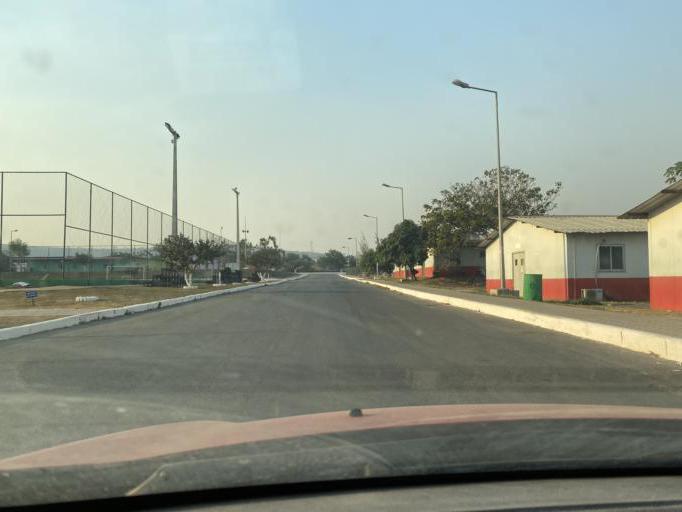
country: AO
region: Cuanza Norte
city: N'dalatando
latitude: -9.7418
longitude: 15.1412
